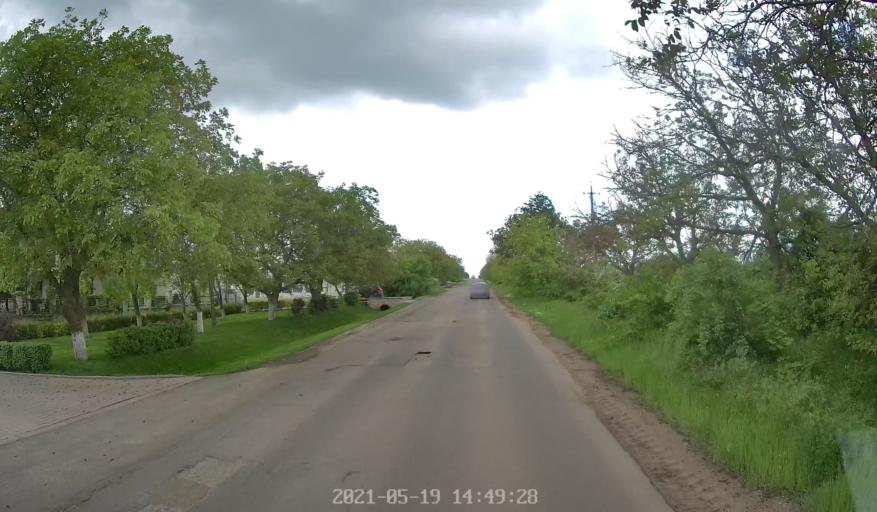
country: MD
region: Chisinau
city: Stauceni
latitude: 47.0502
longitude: 28.9513
